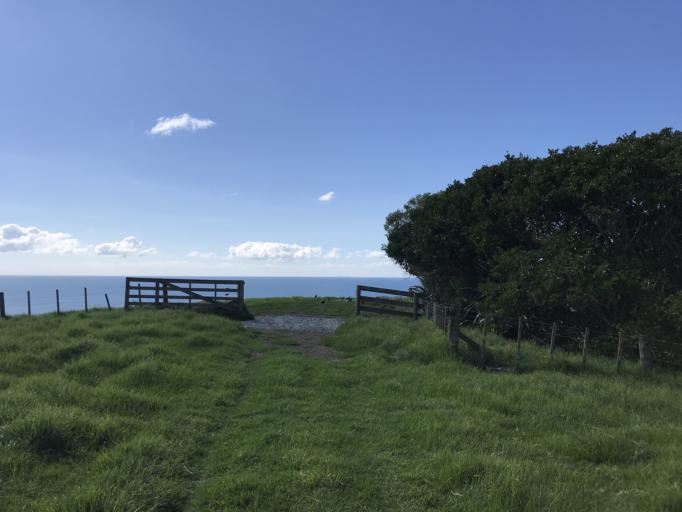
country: NZ
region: Auckland
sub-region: Auckland
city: Warkworth
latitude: -36.3733
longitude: 174.8344
